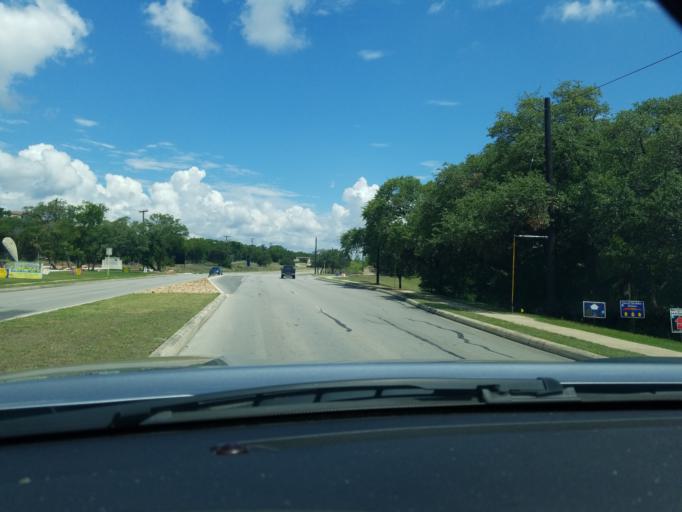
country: US
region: Texas
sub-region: Bexar County
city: Timberwood Park
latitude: 29.6904
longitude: -98.4780
